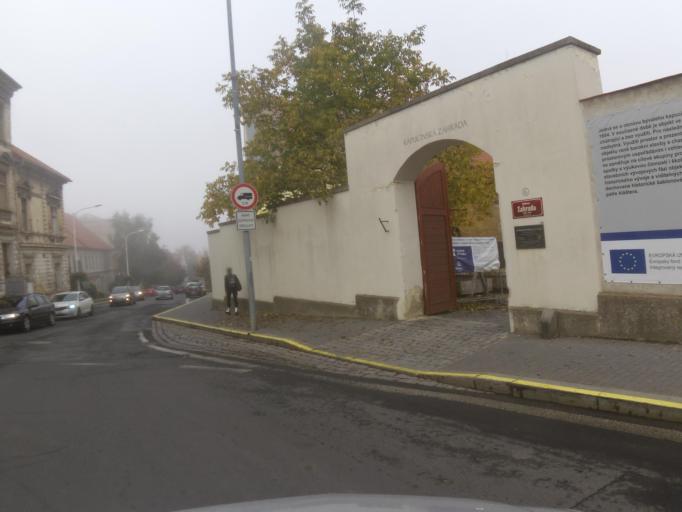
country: CZ
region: Ustecky
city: Zatec
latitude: 50.3246
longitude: 13.5479
